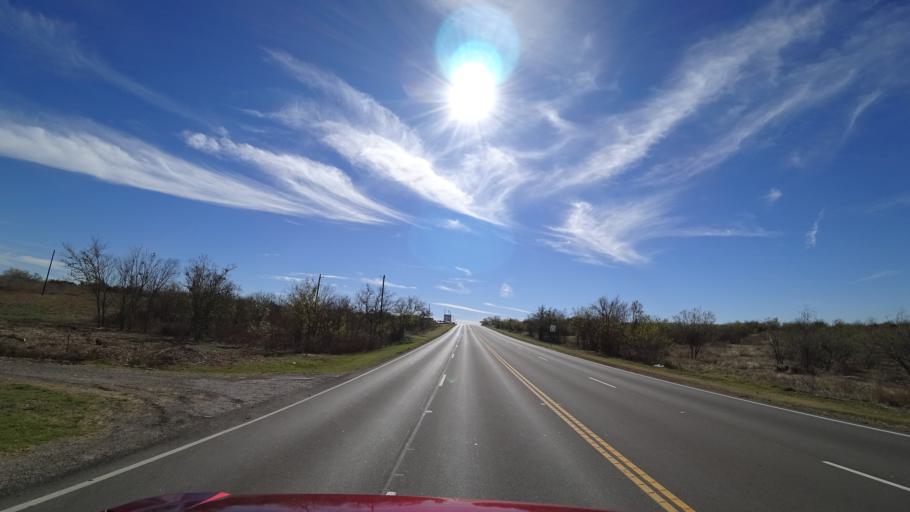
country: US
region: Texas
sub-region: Travis County
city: Onion Creek
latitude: 30.1000
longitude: -97.6942
